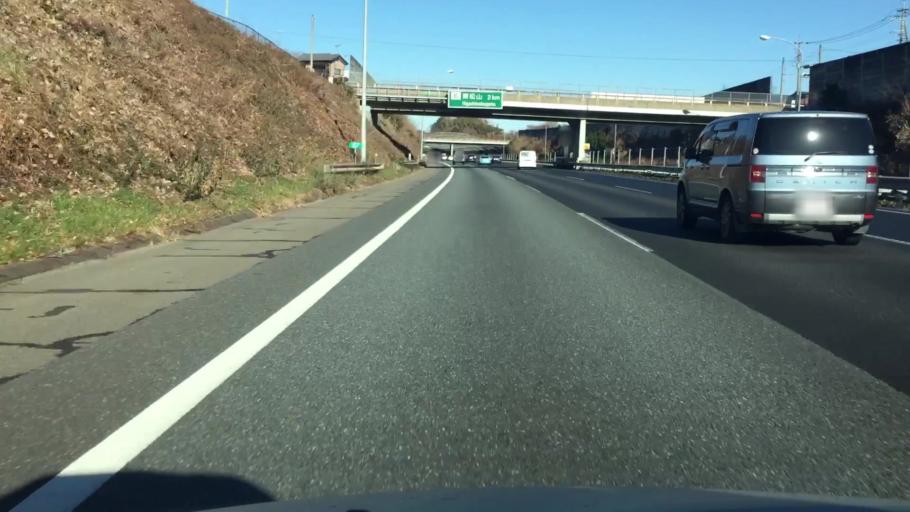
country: JP
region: Saitama
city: Sakado
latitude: 36.0054
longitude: 139.3875
